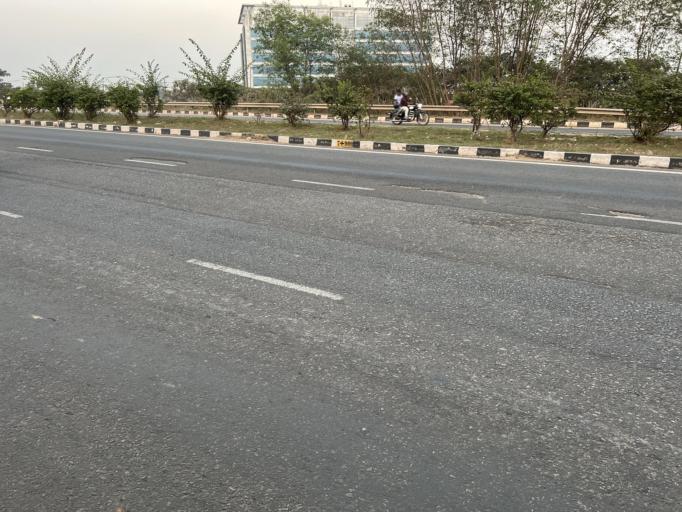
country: IN
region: Odisha
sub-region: Khordha
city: Bhubaneshwar
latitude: 20.3360
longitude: 85.8834
